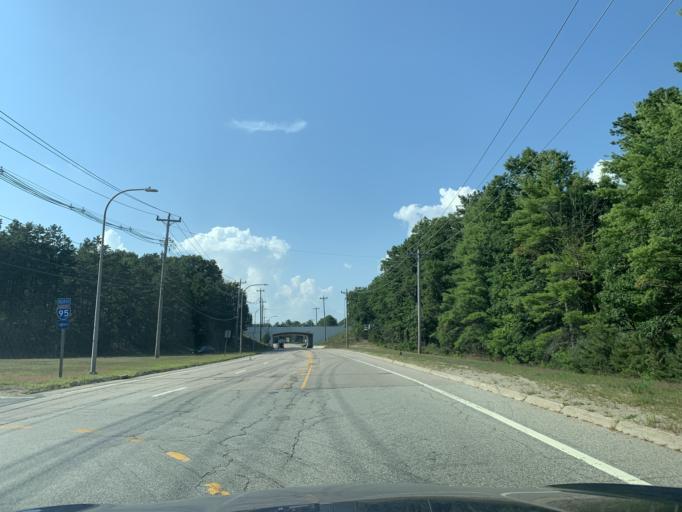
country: US
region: Rhode Island
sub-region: Kent County
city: West Warwick
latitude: 41.6511
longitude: -71.5741
